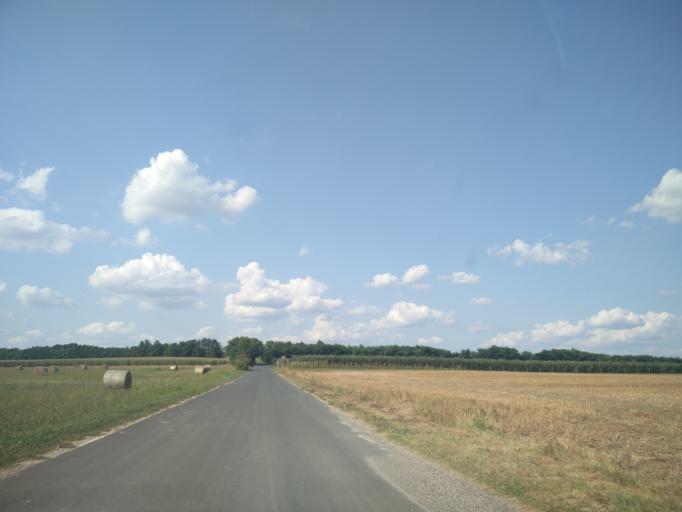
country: HU
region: Zala
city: Zalaegerszeg
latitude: 46.8926
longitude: 16.7929
